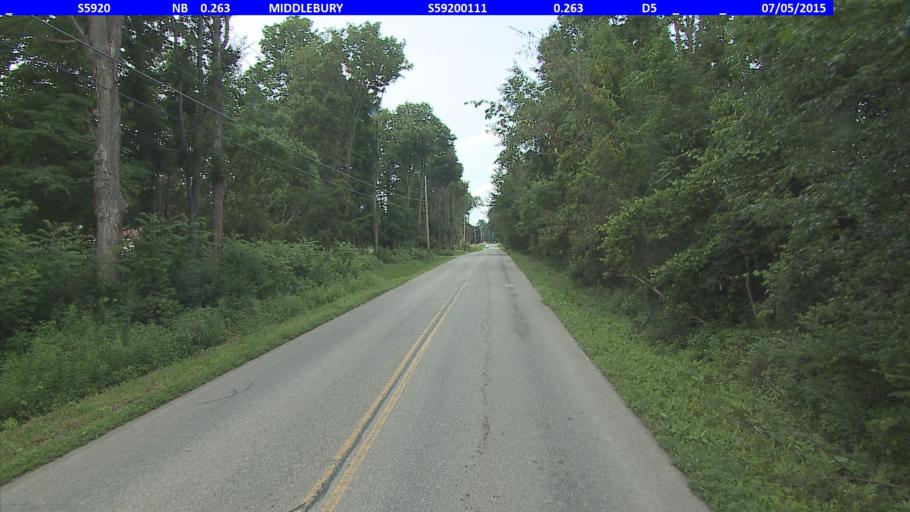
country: US
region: Vermont
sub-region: Addison County
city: Middlebury (village)
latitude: 43.9920
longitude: -73.1348
